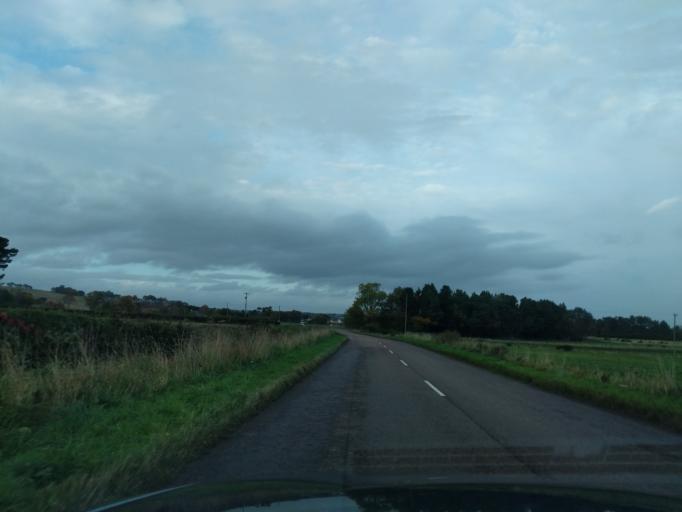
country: GB
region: Scotland
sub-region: Fife
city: Tayport
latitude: 56.4346
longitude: -2.8843
